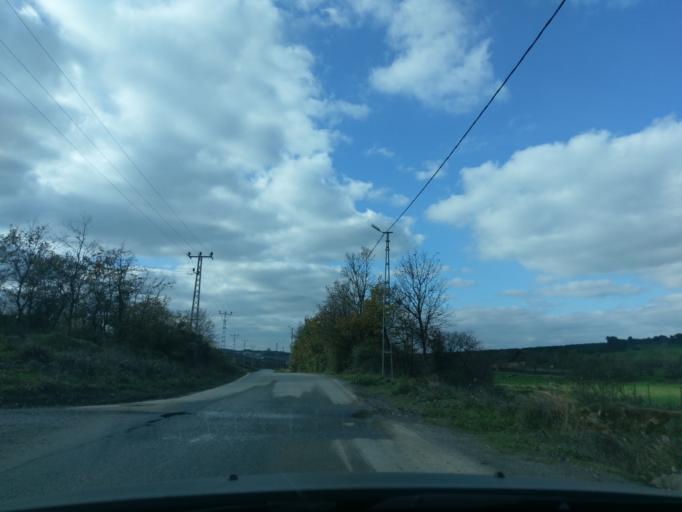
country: TR
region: Istanbul
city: Durusu
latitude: 41.3161
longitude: 28.7111
